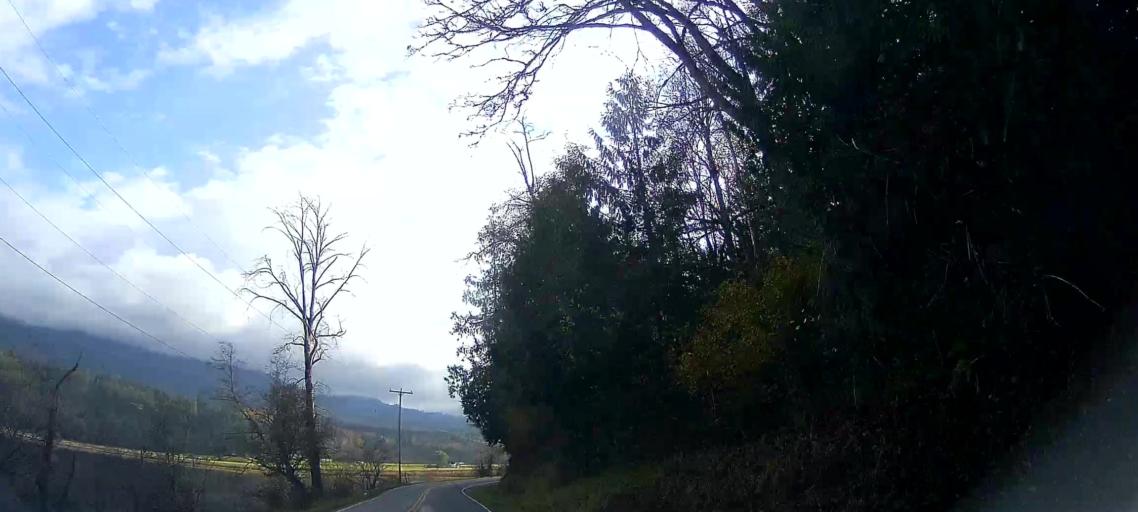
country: US
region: Washington
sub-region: Skagit County
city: Clear Lake
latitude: 48.4477
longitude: -122.2230
